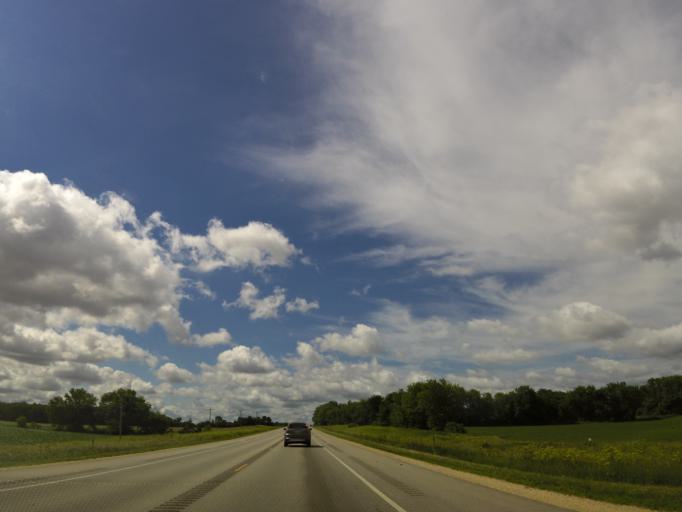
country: US
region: Minnesota
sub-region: Mower County
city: Grand Meadow
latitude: 43.7341
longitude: -92.4793
